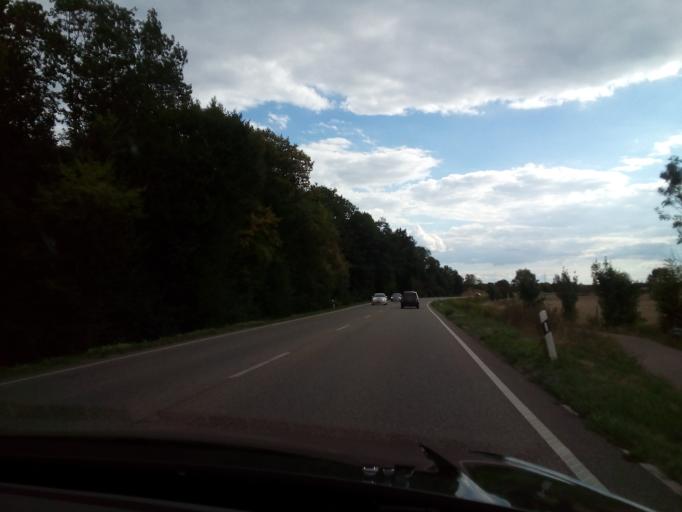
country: DE
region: Baden-Wuerttemberg
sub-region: Freiburg Region
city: Renchen
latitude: 48.5747
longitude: 7.9965
